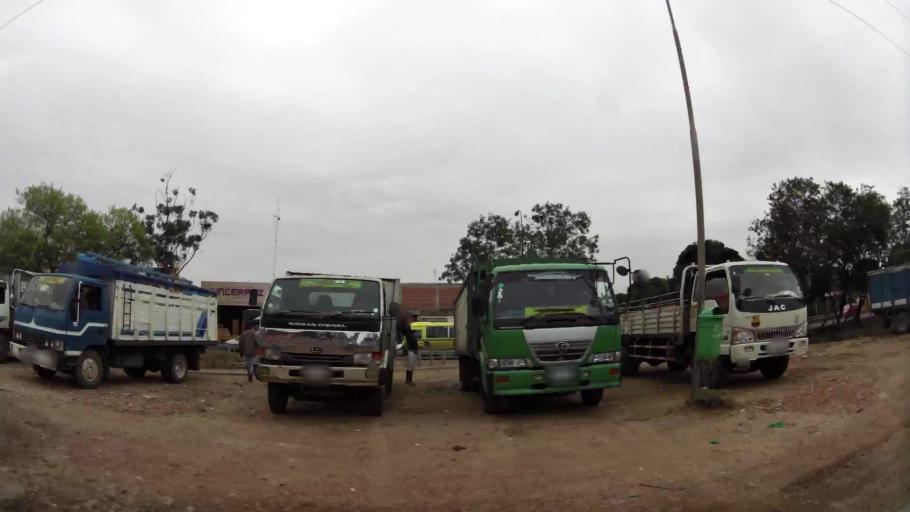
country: BO
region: Santa Cruz
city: Santa Cruz de la Sierra
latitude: -17.7786
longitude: -63.1472
